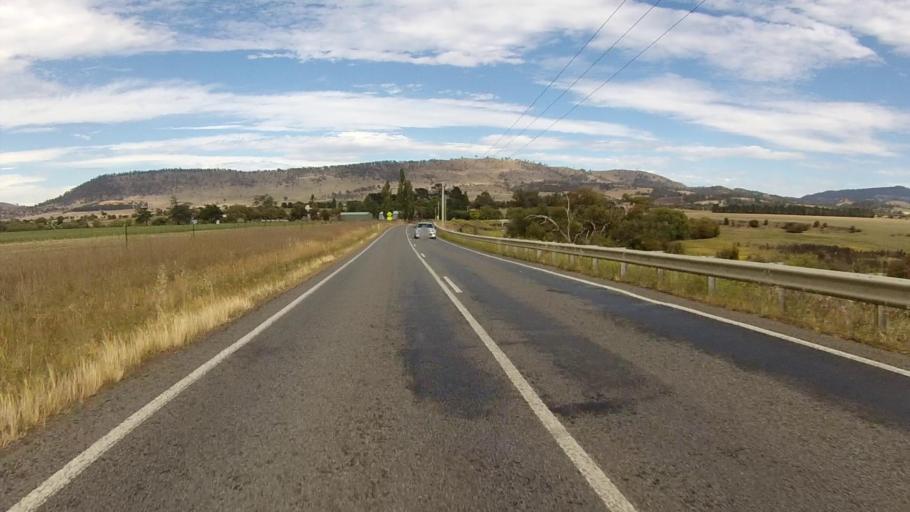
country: AU
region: Tasmania
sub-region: Clarence
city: Cambridge
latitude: -42.6885
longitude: 147.4411
